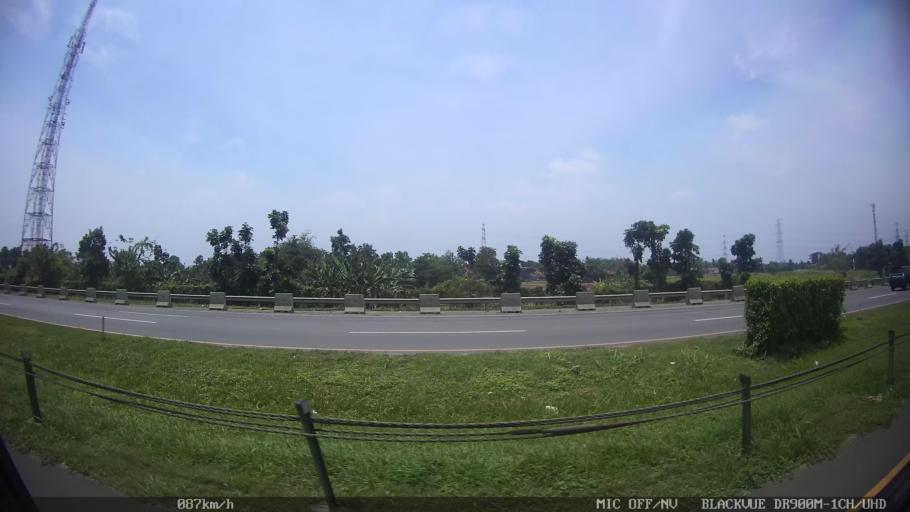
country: ID
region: West Java
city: Kresek
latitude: -6.1896
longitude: 106.4112
